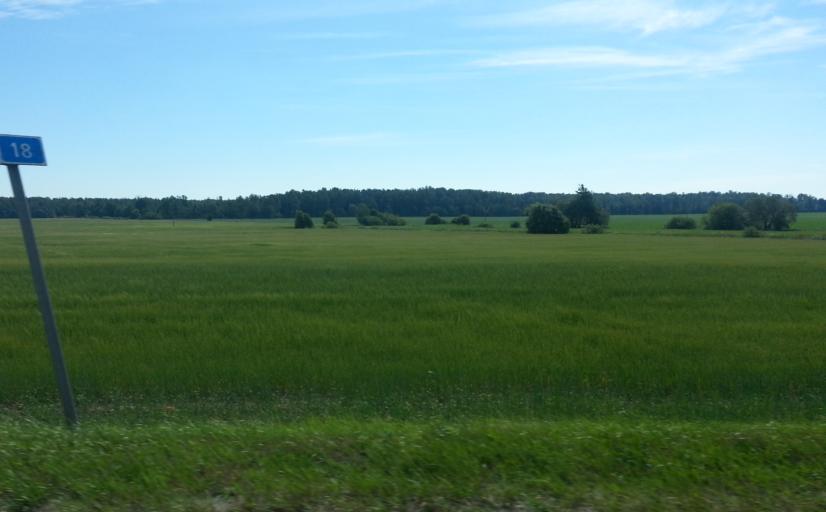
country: LT
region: Panevezys
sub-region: Panevezys City
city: Panevezys
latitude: 55.7902
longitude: 24.3127
